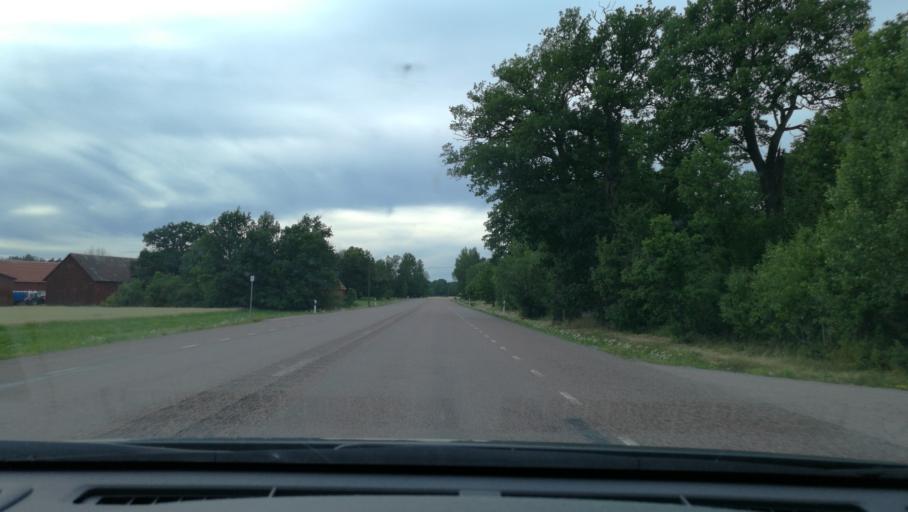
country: SE
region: Vaestmanland
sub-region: Kungsors Kommun
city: Kungsoer
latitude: 59.4403
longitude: 16.0495
